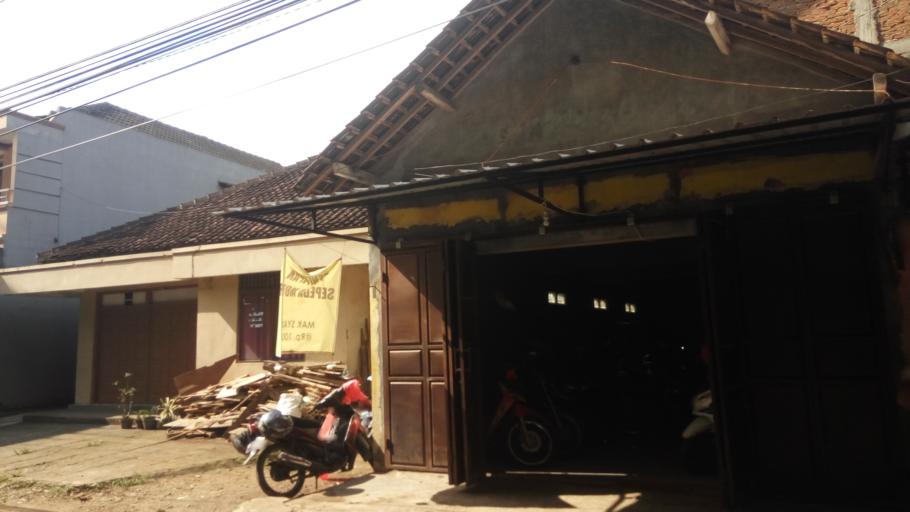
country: ID
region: Central Java
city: Ungaran
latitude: -7.1514
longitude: 110.4169
